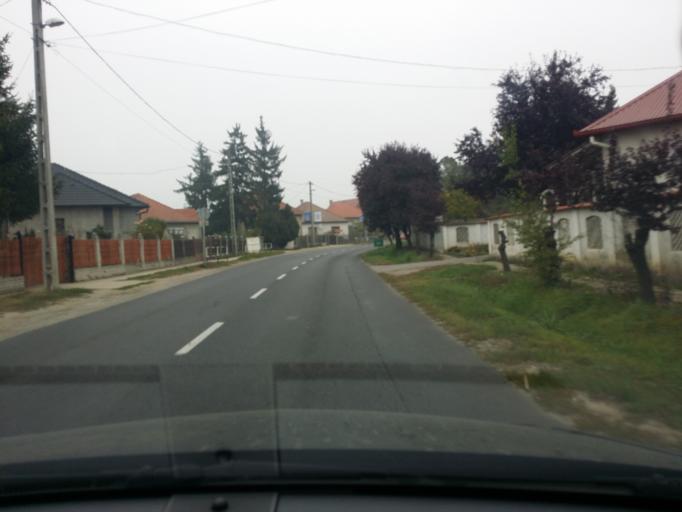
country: HU
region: Szabolcs-Szatmar-Bereg
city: Nyirpazony
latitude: 48.0121
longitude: 21.8296
